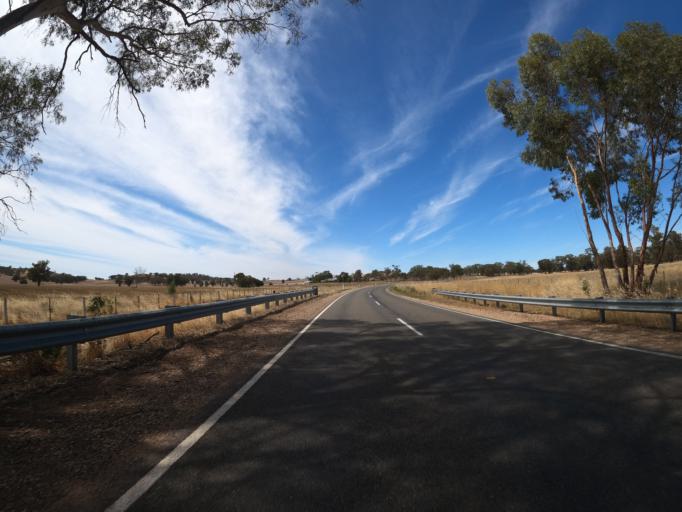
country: AU
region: Victoria
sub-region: Benalla
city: Benalla
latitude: -36.3286
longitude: 145.9613
